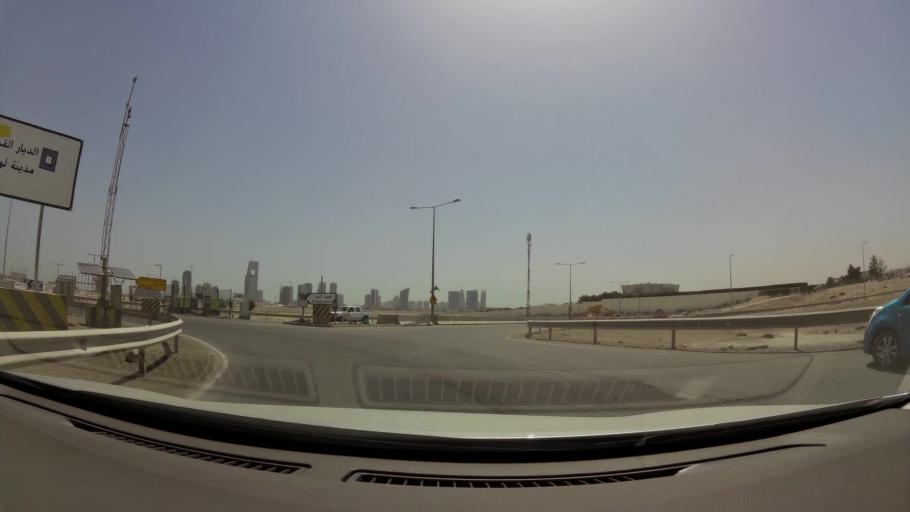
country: QA
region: Baladiyat Umm Salal
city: Umm Salal Muhammad
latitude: 25.3943
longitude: 51.4999
